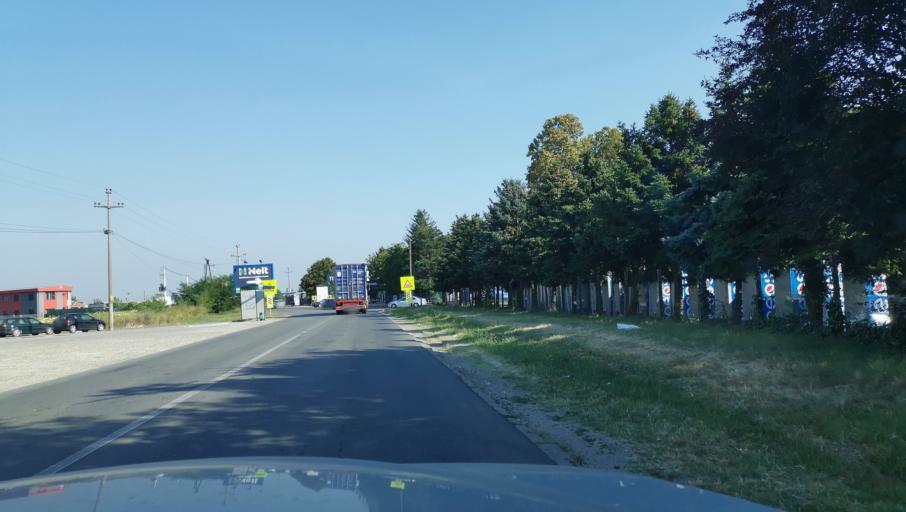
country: RS
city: Dobanovci
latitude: 44.8117
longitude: 20.2421
